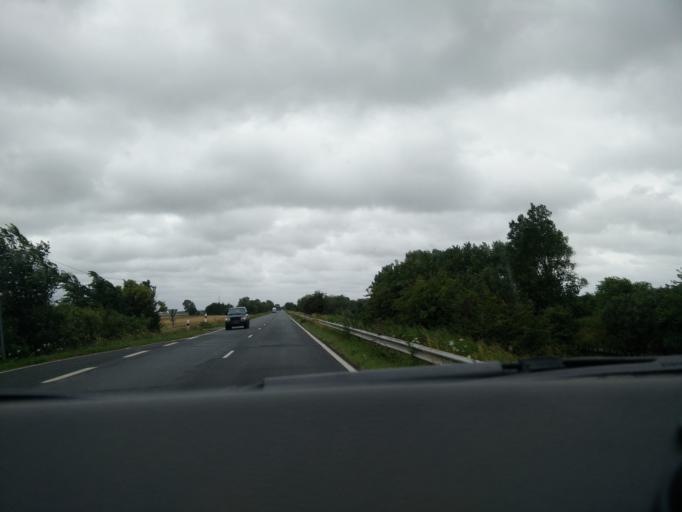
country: FR
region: Nord-Pas-de-Calais
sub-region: Departement du Nord
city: Zuydcoote
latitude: 51.0566
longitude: 2.4876
